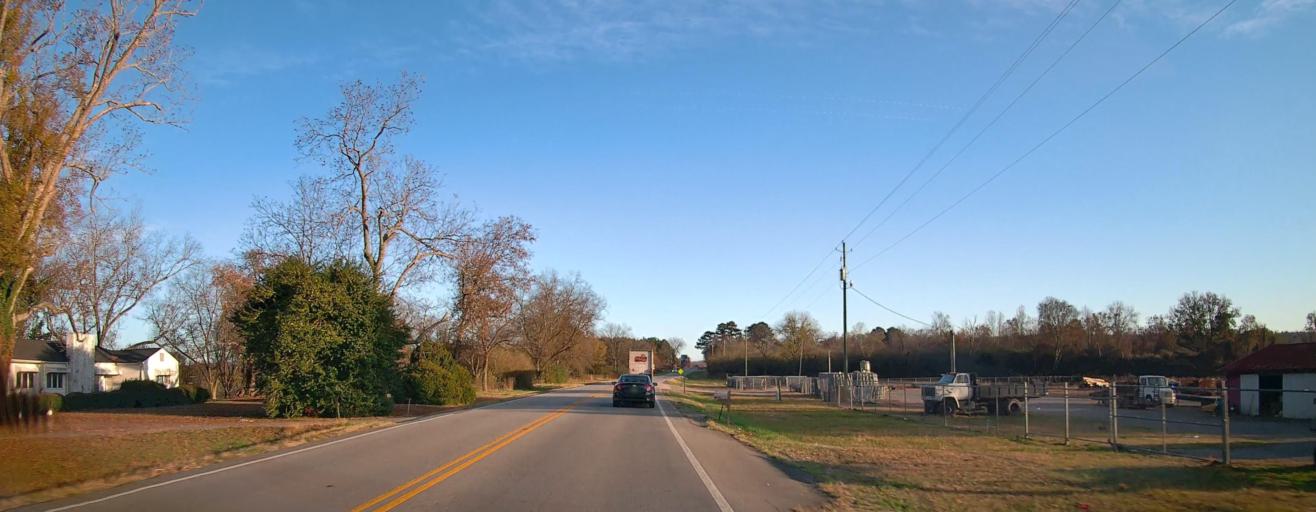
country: US
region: Alabama
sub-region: Blount County
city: Oneonta
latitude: 34.0946
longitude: -86.3564
